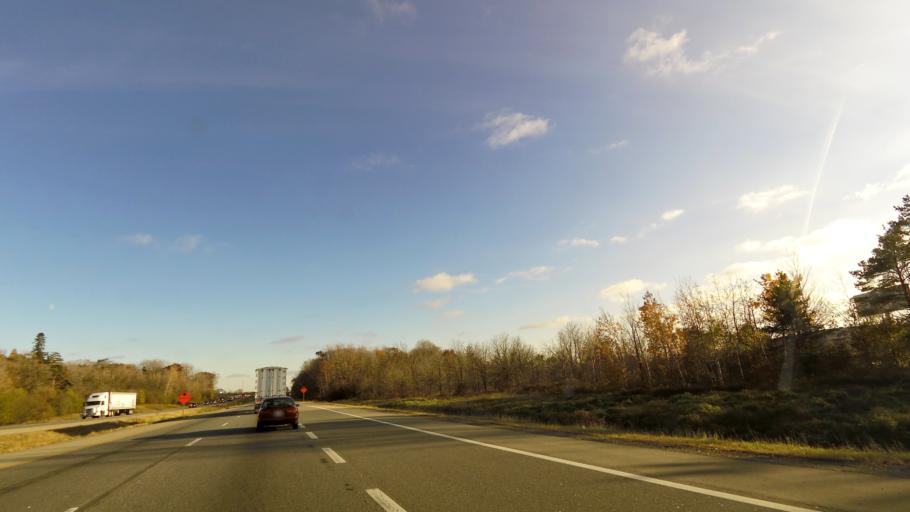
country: CA
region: Ontario
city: Cambridge
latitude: 43.4074
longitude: -80.3849
